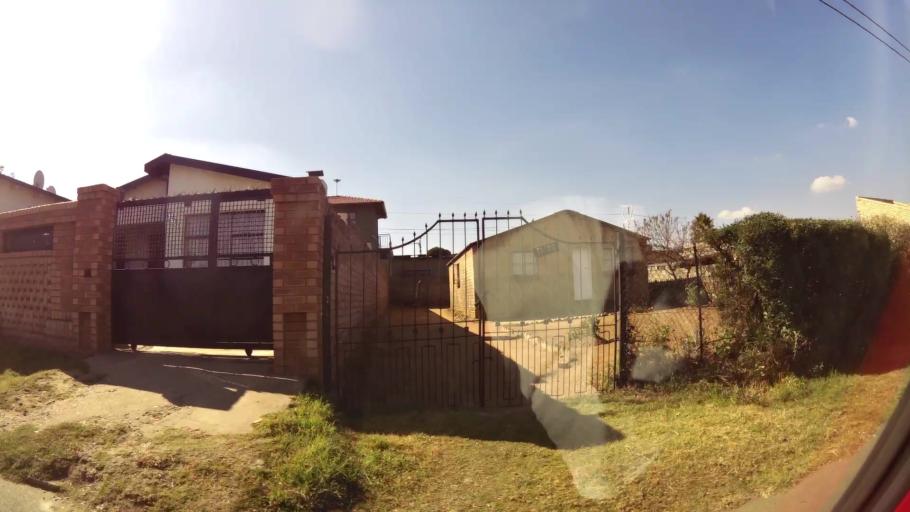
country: ZA
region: Gauteng
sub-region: City of Johannesburg Metropolitan Municipality
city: Soweto
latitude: -26.2424
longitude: 27.8995
